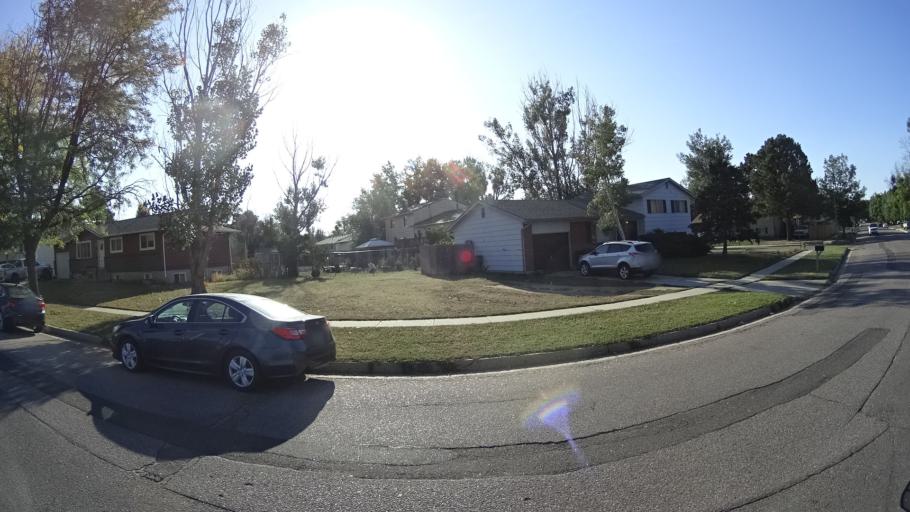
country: US
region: Colorado
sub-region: El Paso County
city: Cimarron Hills
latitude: 38.8925
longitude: -104.7473
